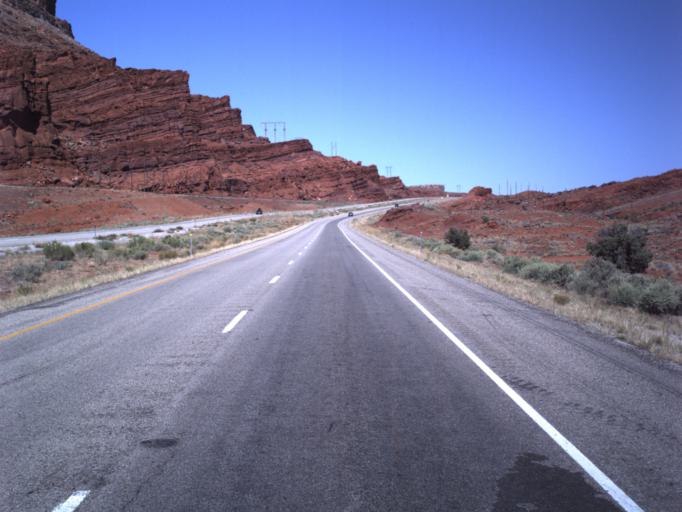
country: US
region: Utah
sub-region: Grand County
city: Moab
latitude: 38.6317
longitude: -109.6578
